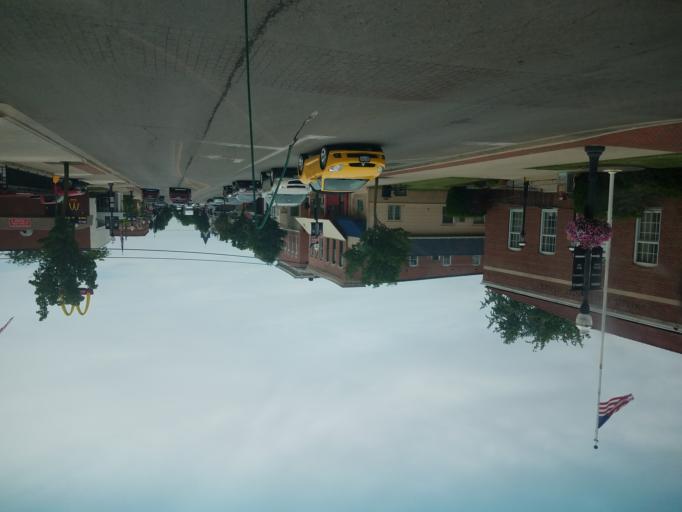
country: US
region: Ohio
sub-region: Hardin County
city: Ada
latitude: 40.7694
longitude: -83.8231
